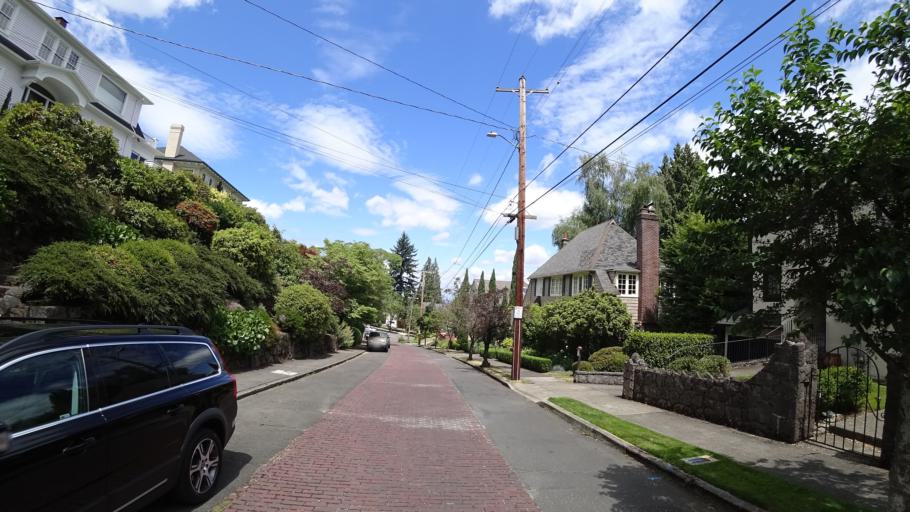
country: US
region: Oregon
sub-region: Multnomah County
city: Portland
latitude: 45.5286
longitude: -122.7084
